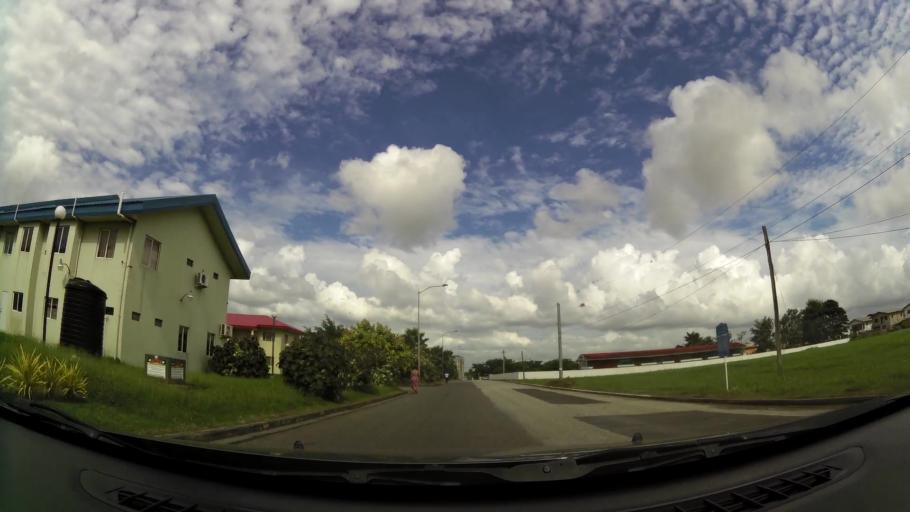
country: TT
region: Chaguanas
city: Chaguanas
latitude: 10.5053
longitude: -61.3997
